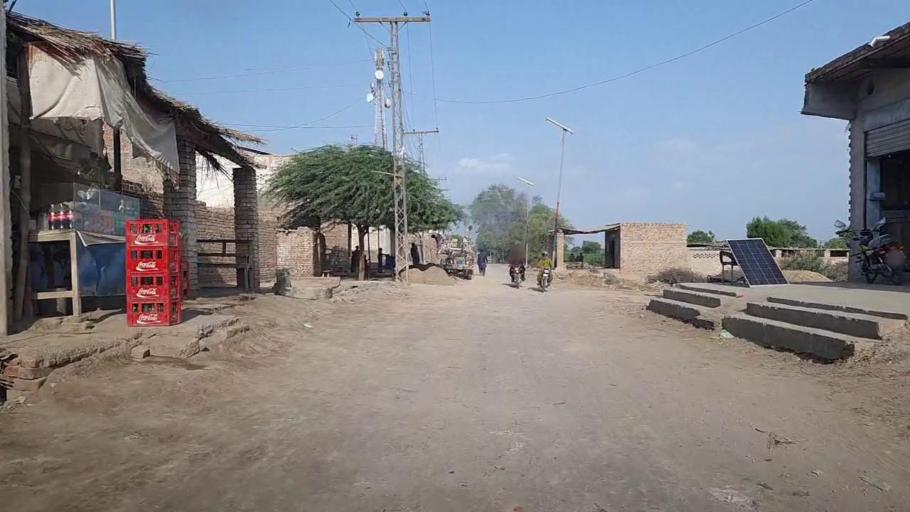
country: PK
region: Sindh
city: Khairpur
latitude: 28.0768
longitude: 69.7965
